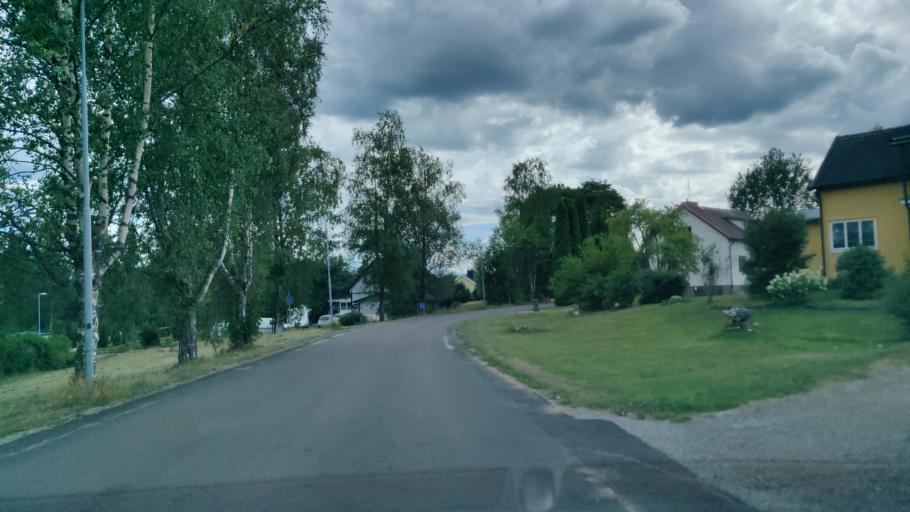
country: SE
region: Vaermland
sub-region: Hagfors Kommun
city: Hagfors
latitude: 60.0433
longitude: 13.6775
